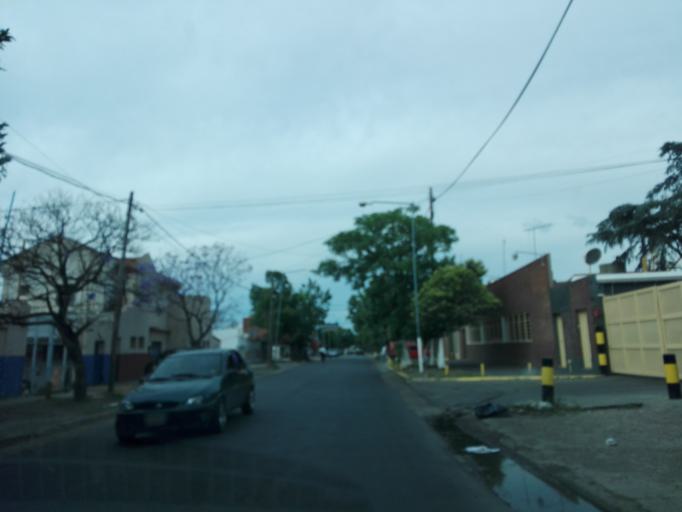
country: AR
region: Buenos Aires
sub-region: Partido de Lanus
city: Lanus
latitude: -34.7049
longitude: -58.3685
